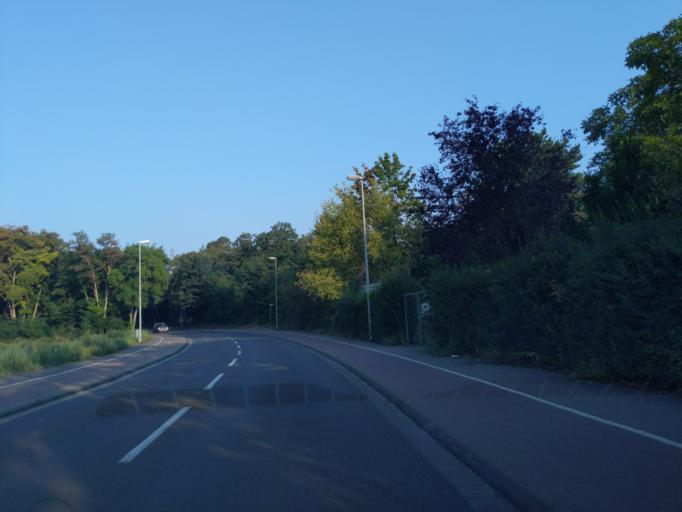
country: DE
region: Rheinland-Pfalz
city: Ingelheim am Rhein
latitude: 49.9871
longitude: 8.0474
